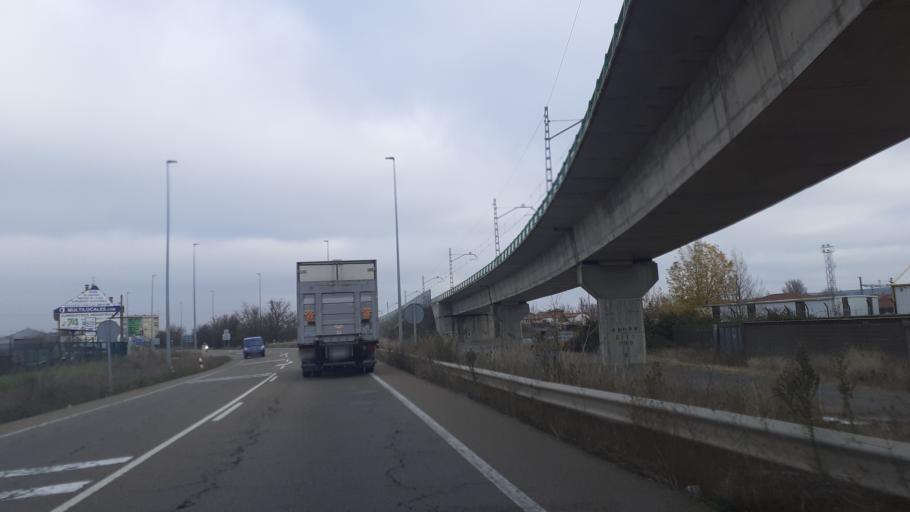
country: ES
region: Castille and Leon
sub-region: Provincia de Leon
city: Onzonilla
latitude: 42.5584
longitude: -5.5818
